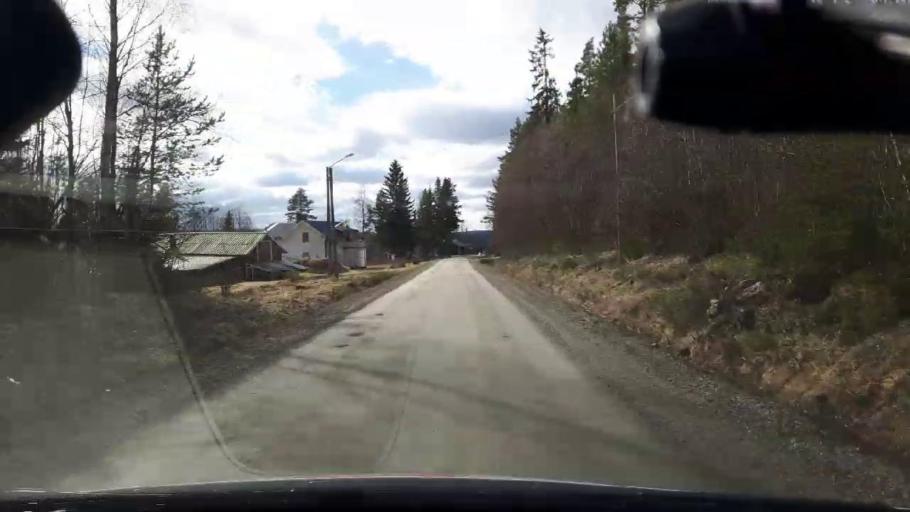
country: SE
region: Jaemtland
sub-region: Bergs Kommun
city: Hoverberg
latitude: 62.7112
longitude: 14.6990
